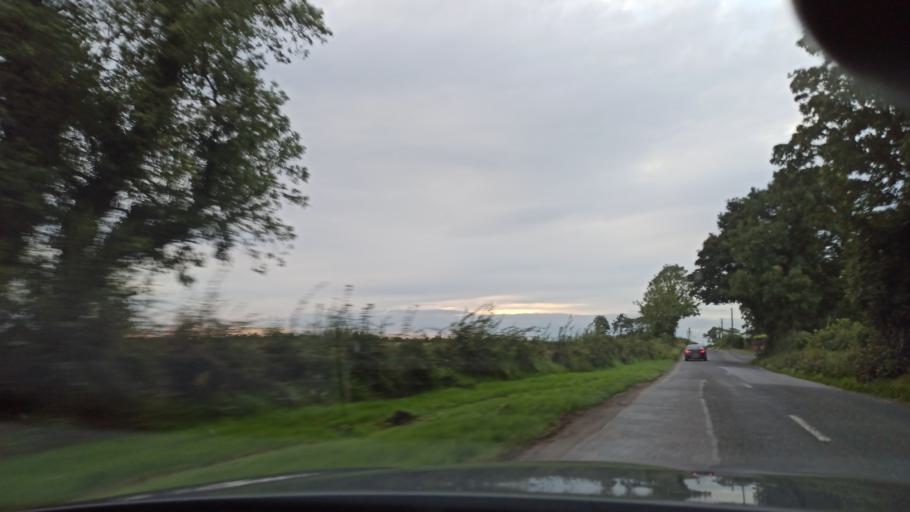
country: IE
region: Munster
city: Cashel
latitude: 52.4951
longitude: -7.8668
